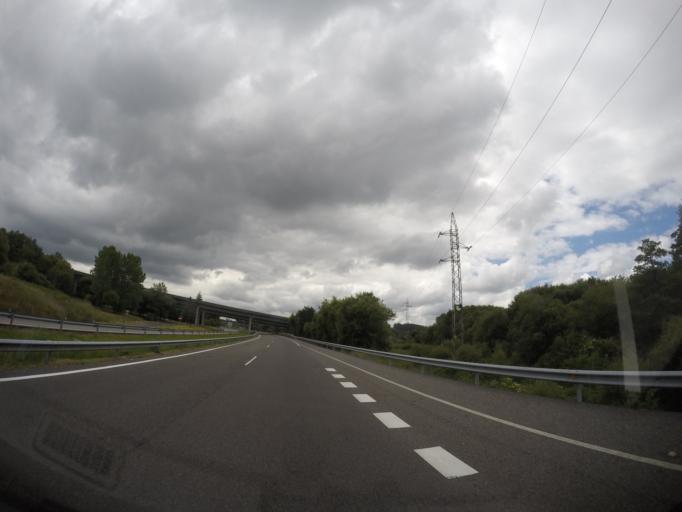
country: ES
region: Galicia
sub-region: Provincia da Coruna
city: Betanzos
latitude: 43.2631
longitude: -8.2542
